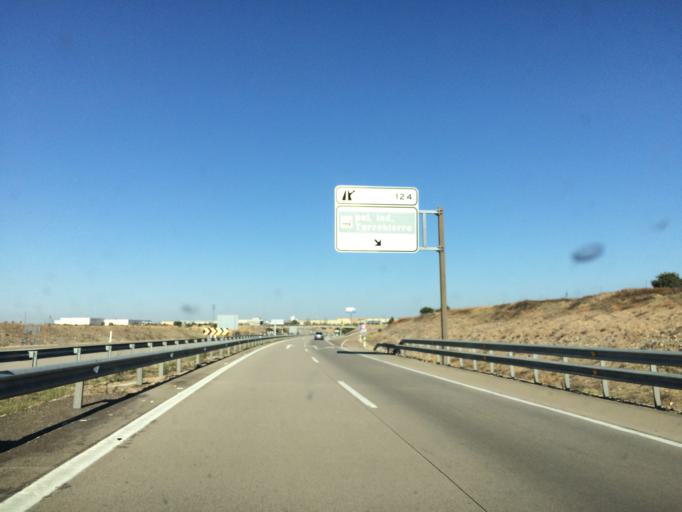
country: ES
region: Castille-La Mancha
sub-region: Province of Toledo
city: Mejorada
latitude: 39.9579
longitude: -4.9111
